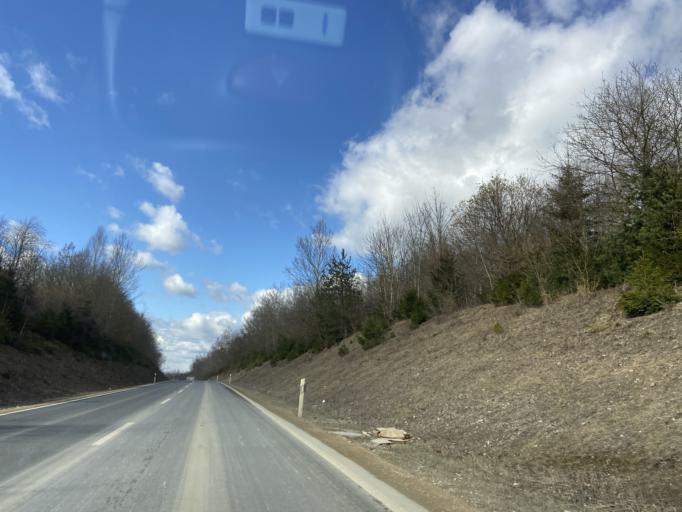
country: DE
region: Baden-Wuerttemberg
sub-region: Tuebingen Region
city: Ostrach
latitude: 47.9534
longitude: 9.3979
